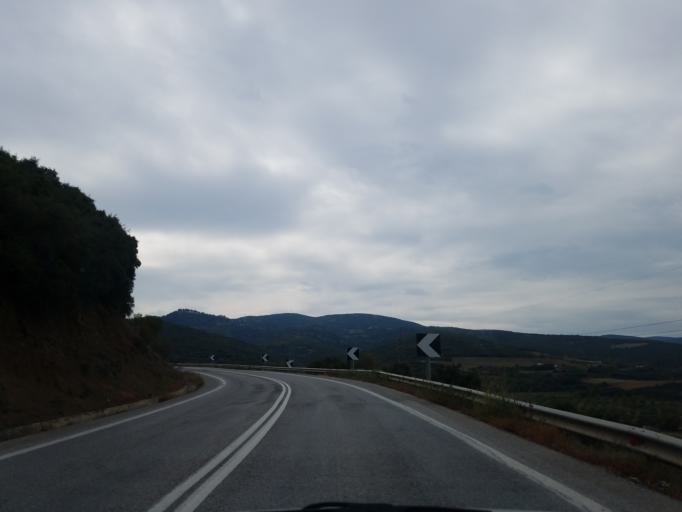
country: GR
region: Central Greece
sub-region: Nomos Fthiotidos
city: Domokos
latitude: 39.1549
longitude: 22.2952
